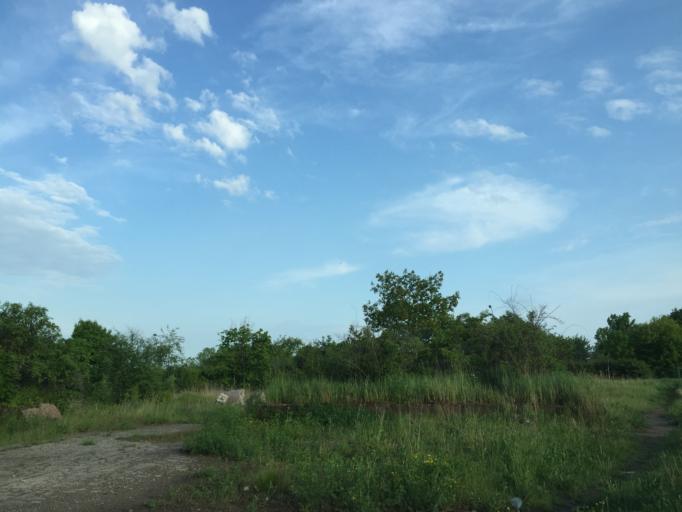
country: LT
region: Klaipedos apskritis
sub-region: Klaipeda
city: Klaipeda
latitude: 55.7536
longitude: 21.1332
